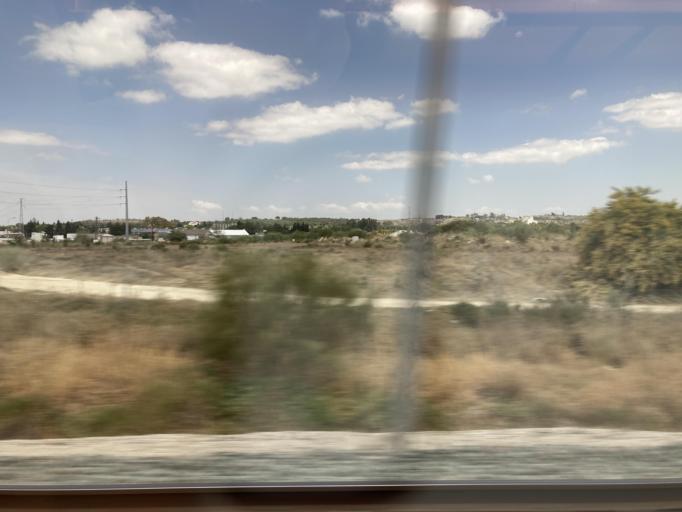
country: ES
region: Andalusia
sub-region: Provincia de Cadiz
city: El Puerto de Santa Maria
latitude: 36.6161
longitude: -6.2013
